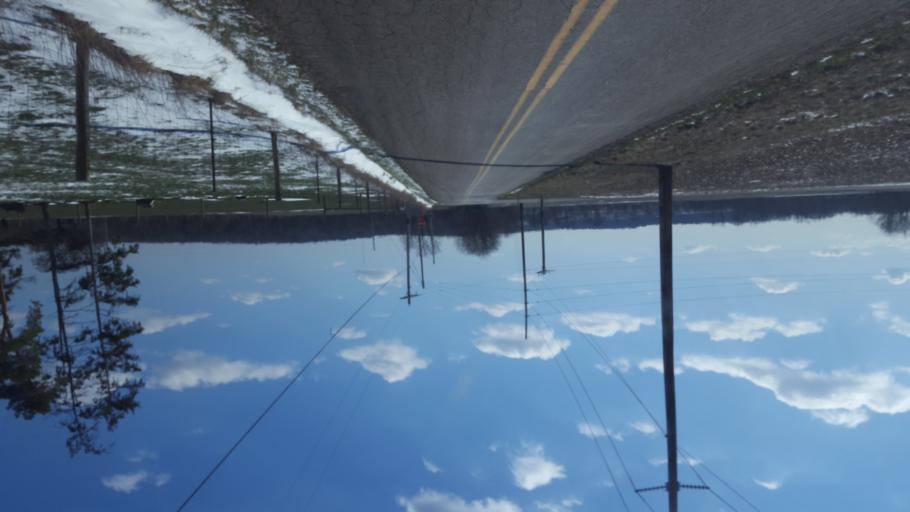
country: US
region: Ohio
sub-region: Licking County
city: Utica
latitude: 40.2680
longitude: -82.4758
